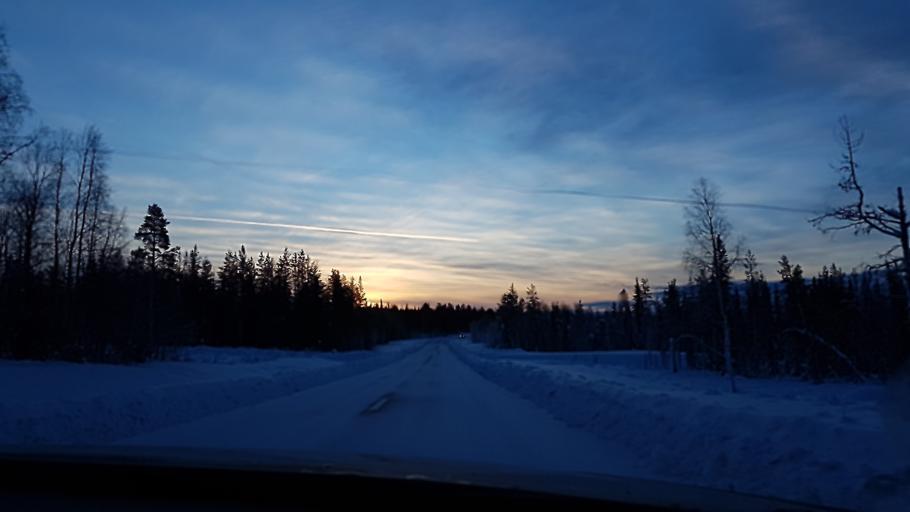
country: SE
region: Norrbotten
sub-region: Jokkmokks Kommun
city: Jokkmokk
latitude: 66.0845
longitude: 20.0727
